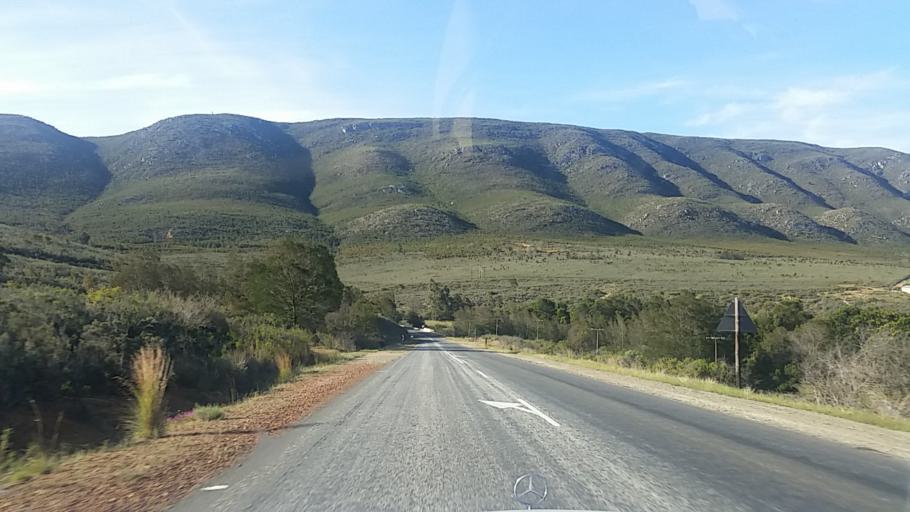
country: ZA
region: Western Cape
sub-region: Eden District Municipality
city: Knysna
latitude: -33.7652
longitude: 22.9623
